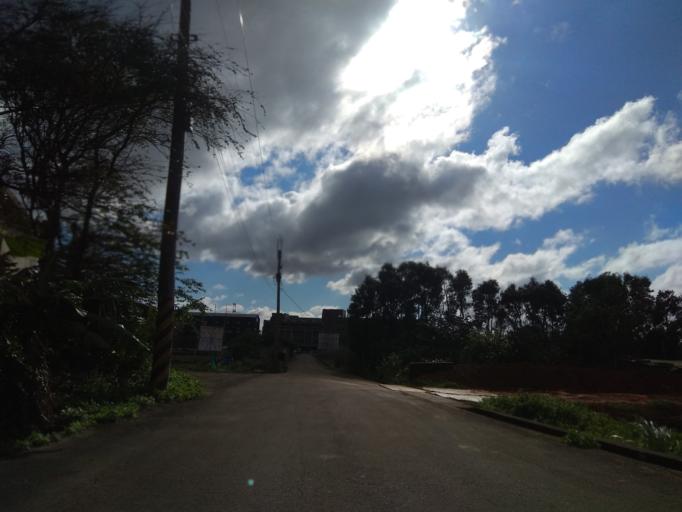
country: TW
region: Taiwan
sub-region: Hsinchu
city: Zhubei
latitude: 24.9707
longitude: 121.0888
